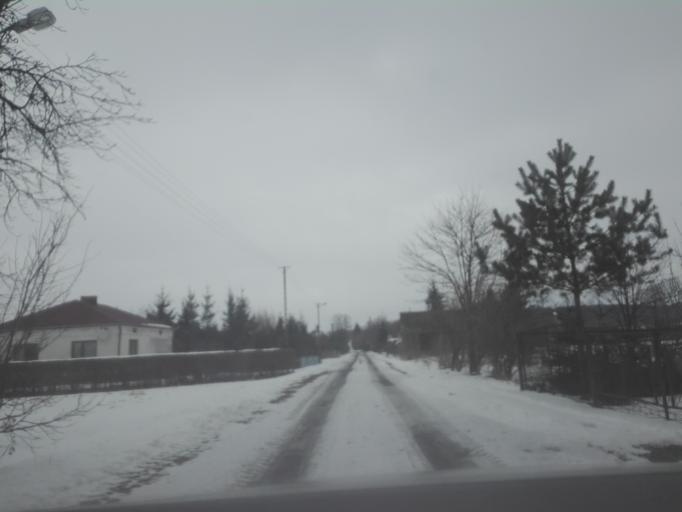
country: PL
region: Lublin Voivodeship
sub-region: Powiat hrubieszowski
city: Horodlo
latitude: 50.8412
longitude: 24.0114
